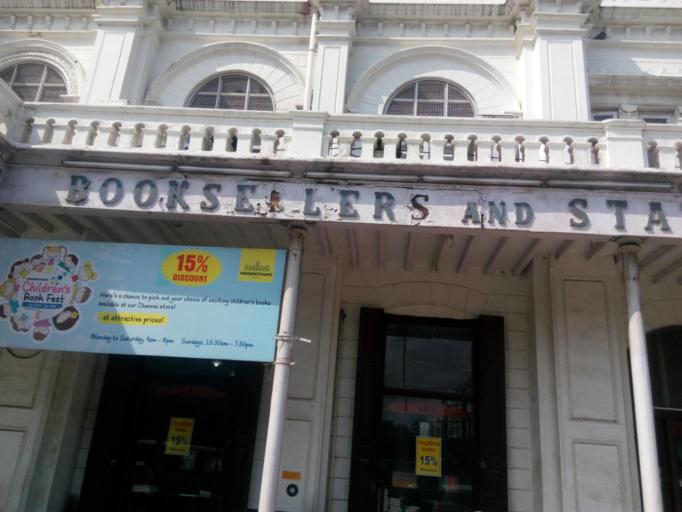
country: IN
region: Tamil Nadu
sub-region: Chennai
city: Chennai
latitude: 13.0652
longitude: 80.2667
